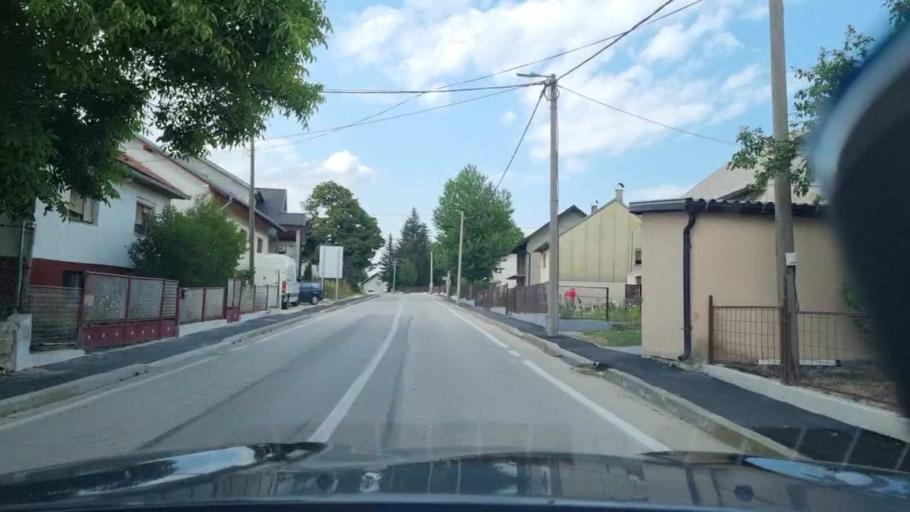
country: BA
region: Federation of Bosnia and Herzegovina
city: Glamoc
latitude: 44.0459
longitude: 16.8569
